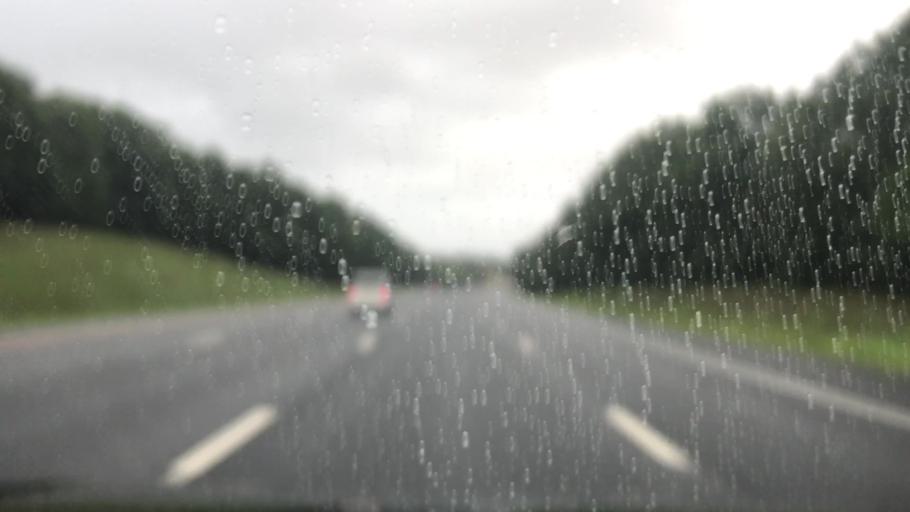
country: US
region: New Jersey
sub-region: Monmouth County
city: Shark River Hills
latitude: 40.2296
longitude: -74.0945
